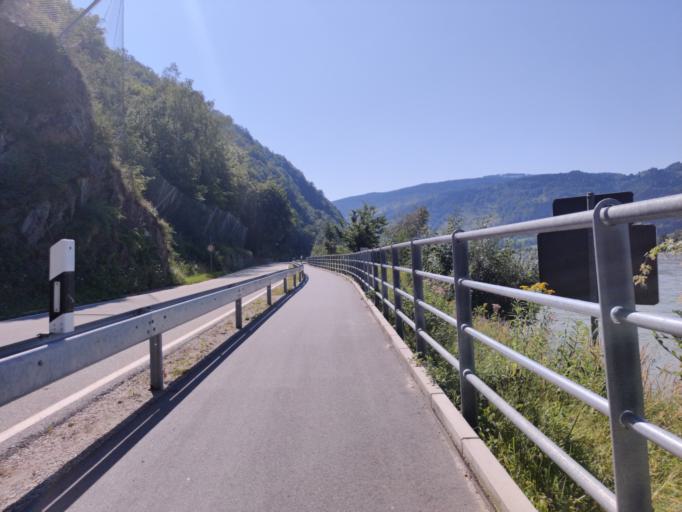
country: DE
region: Bavaria
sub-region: Lower Bavaria
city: Obernzell
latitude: 48.5477
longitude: 13.6564
